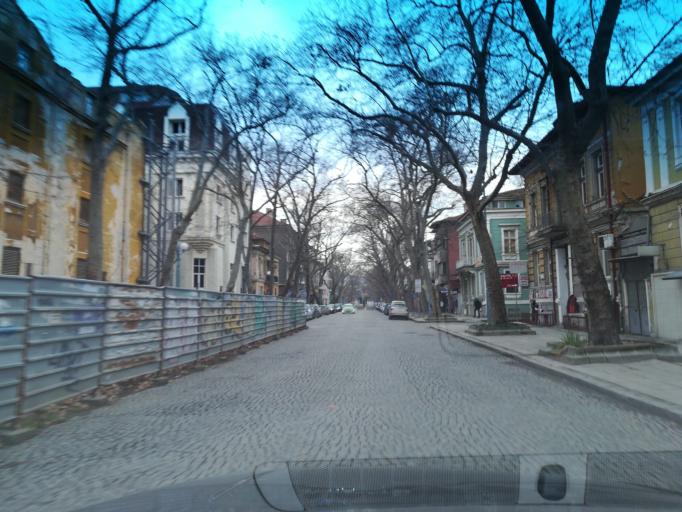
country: BG
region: Plovdiv
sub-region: Obshtina Plovdiv
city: Plovdiv
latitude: 42.1382
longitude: 24.7452
